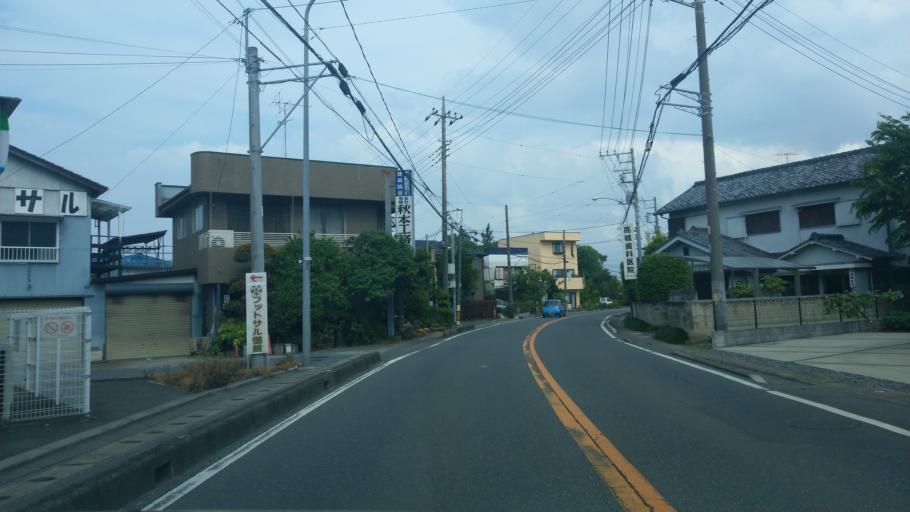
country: JP
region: Saitama
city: Saitama
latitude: 35.9095
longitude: 139.6732
